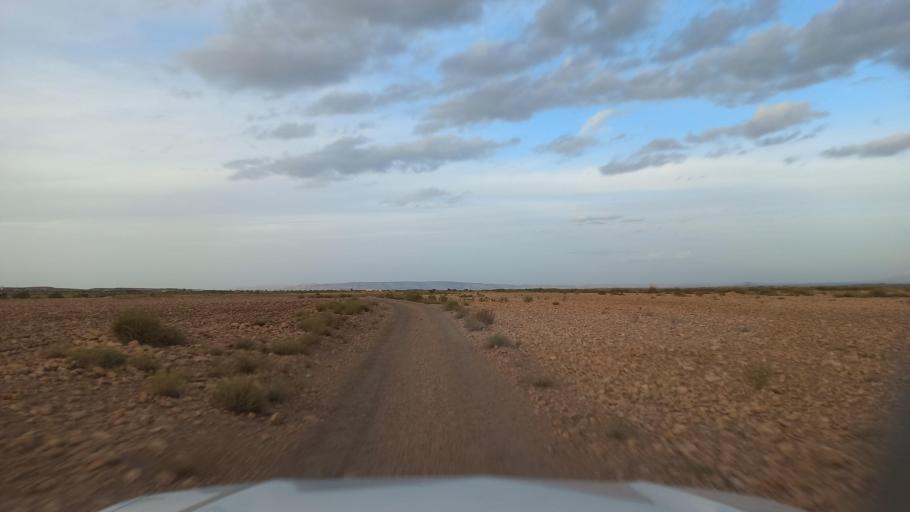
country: TN
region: Al Qasrayn
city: Sbiba
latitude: 35.4242
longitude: 9.0776
